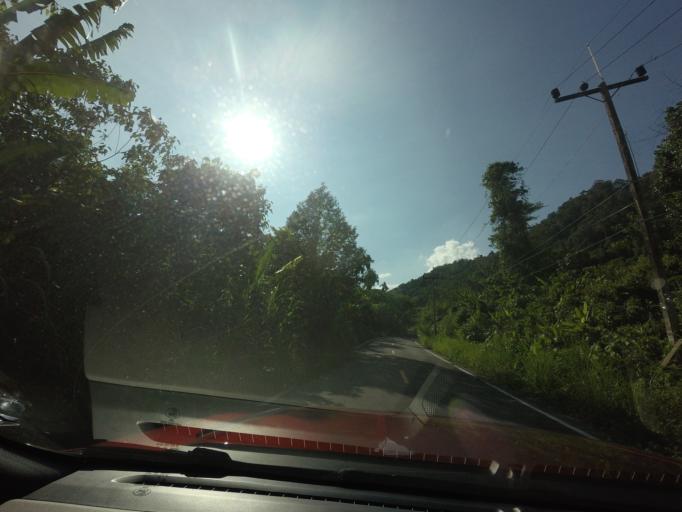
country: TH
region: Yala
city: Than To
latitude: 6.0715
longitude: 101.3473
